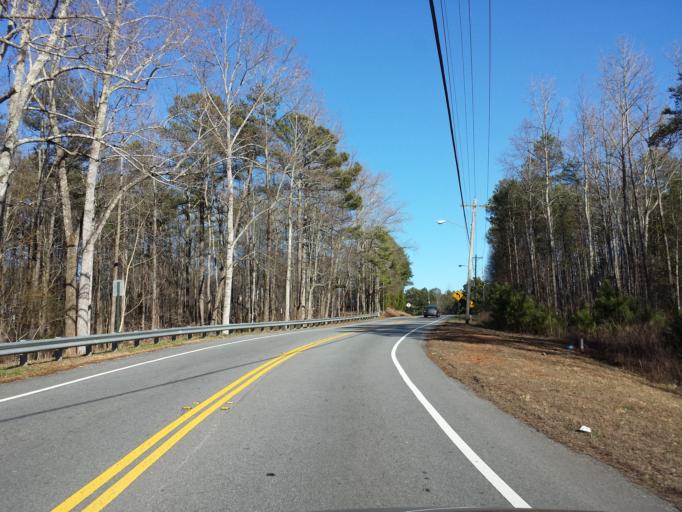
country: US
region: Georgia
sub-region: Cobb County
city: Kennesaw
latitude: 33.9652
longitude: -84.6576
